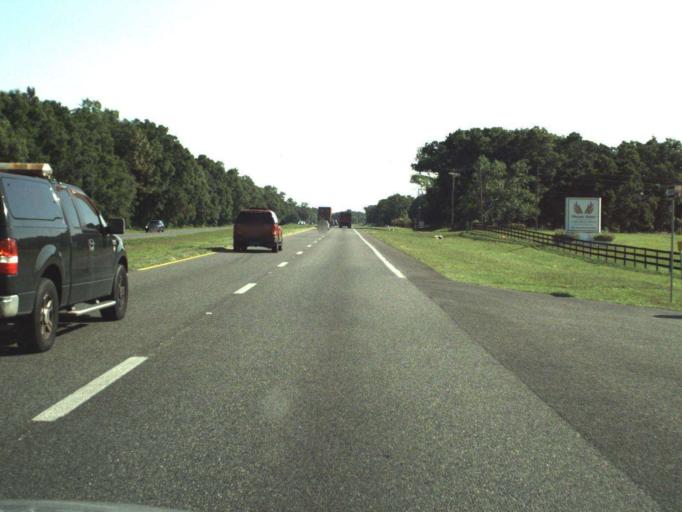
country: US
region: Florida
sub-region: Marion County
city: Citra
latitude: 29.3771
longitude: -82.1307
